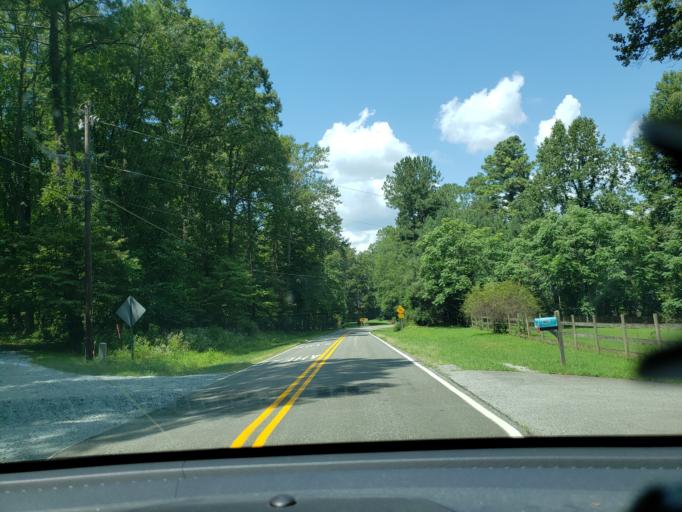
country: US
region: North Carolina
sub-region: Orange County
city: Hillsborough
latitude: 36.0693
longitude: -78.9979
